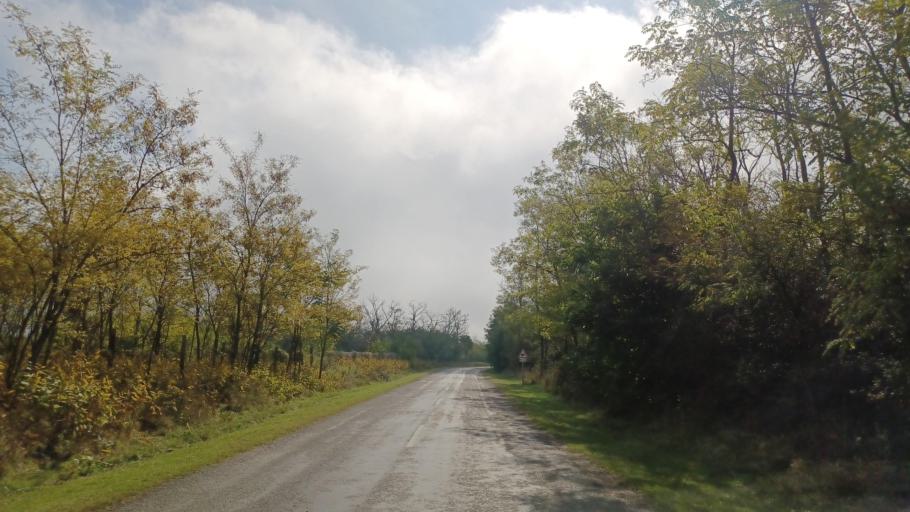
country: HU
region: Tolna
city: Pincehely
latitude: 46.6607
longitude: 18.4987
